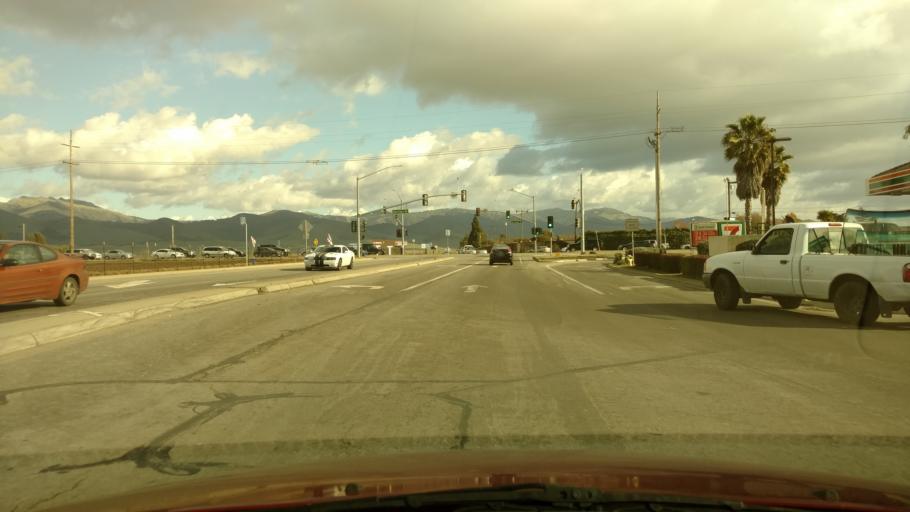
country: US
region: California
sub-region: Monterey County
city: Salinas
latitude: 36.7157
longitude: -121.6247
